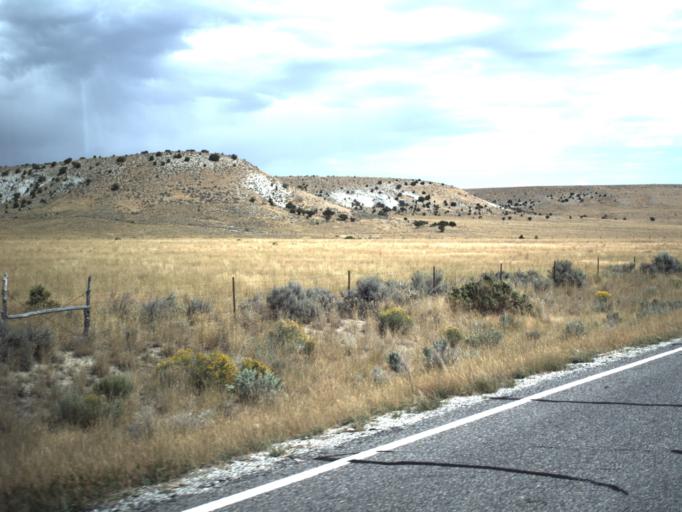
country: US
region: Idaho
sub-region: Cassia County
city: Burley
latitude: 41.8163
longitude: -113.2362
